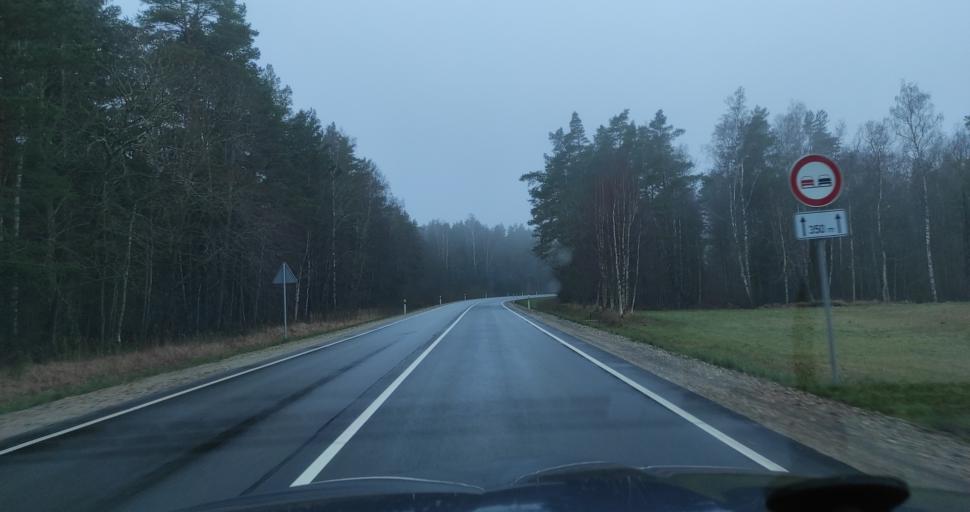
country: LV
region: Pavilostas
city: Pavilosta
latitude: 56.9210
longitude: 21.2608
